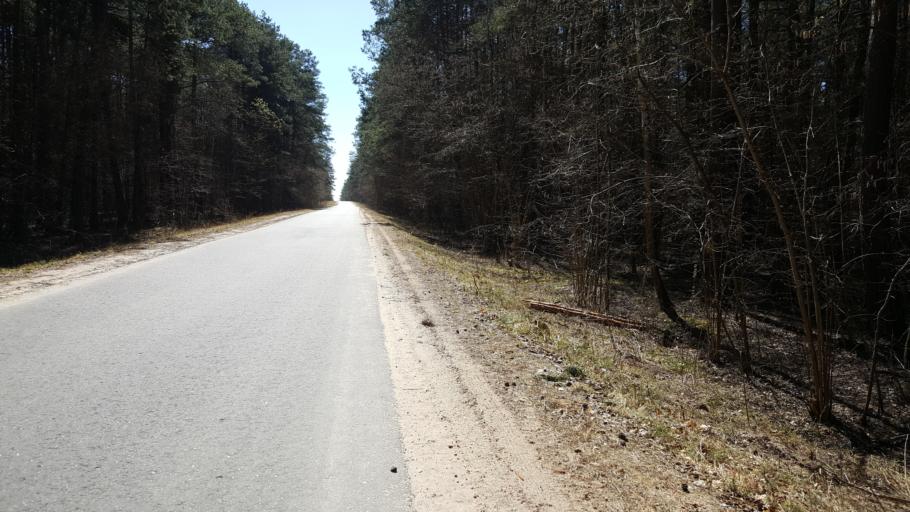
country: BY
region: Brest
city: Kamyanyets
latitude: 52.3410
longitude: 23.8221
